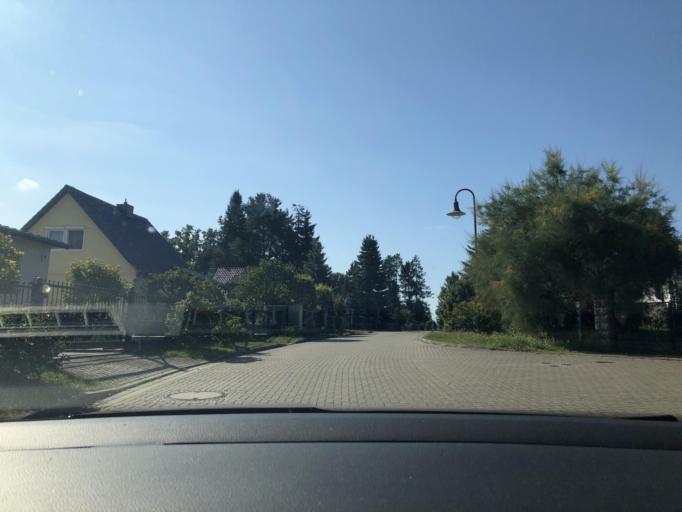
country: DE
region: Brandenburg
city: Erkner
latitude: 52.4141
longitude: 13.7391
